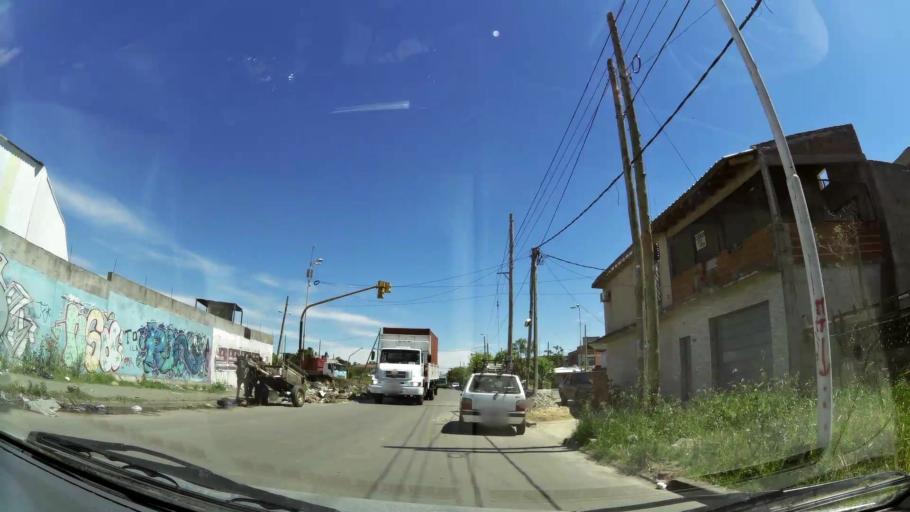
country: AR
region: Buenos Aires
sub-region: Partido de Lanus
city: Lanus
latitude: -34.7363
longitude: -58.3438
